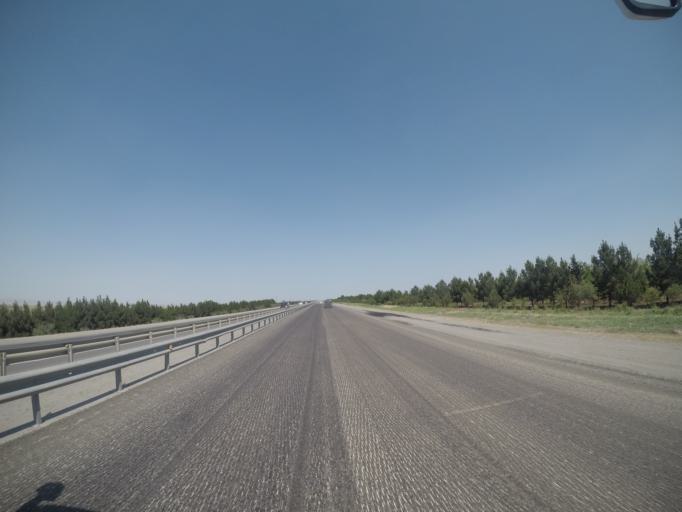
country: AZ
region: Haciqabul
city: Haciqabul
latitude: 40.0458
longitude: 49.0083
